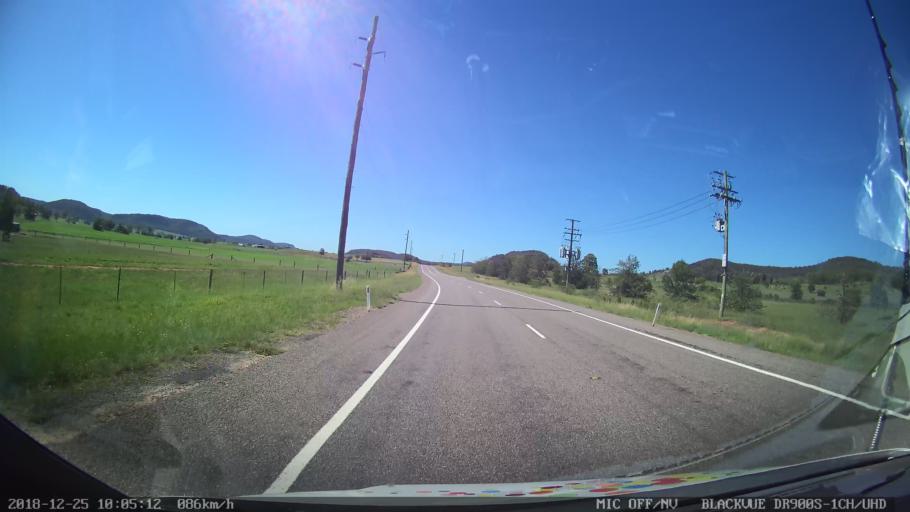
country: AU
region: New South Wales
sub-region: Upper Hunter Shire
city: Merriwa
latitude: -32.2440
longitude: 150.4857
